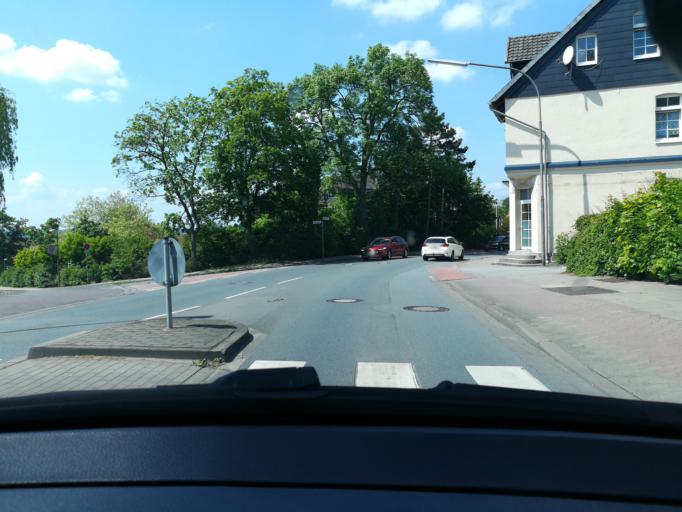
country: DE
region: North Rhine-Westphalia
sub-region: Regierungsbezirk Detmold
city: Herford
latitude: 52.1155
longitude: 8.6884
